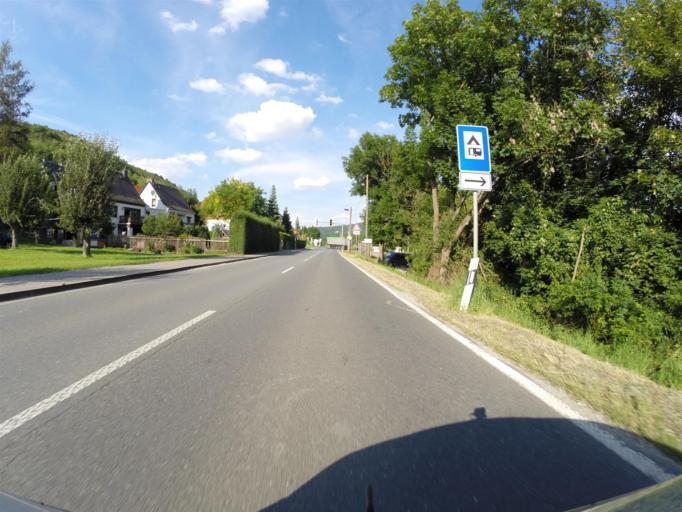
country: DE
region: Thuringia
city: Neuengonna
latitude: 50.9770
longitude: 11.6443
